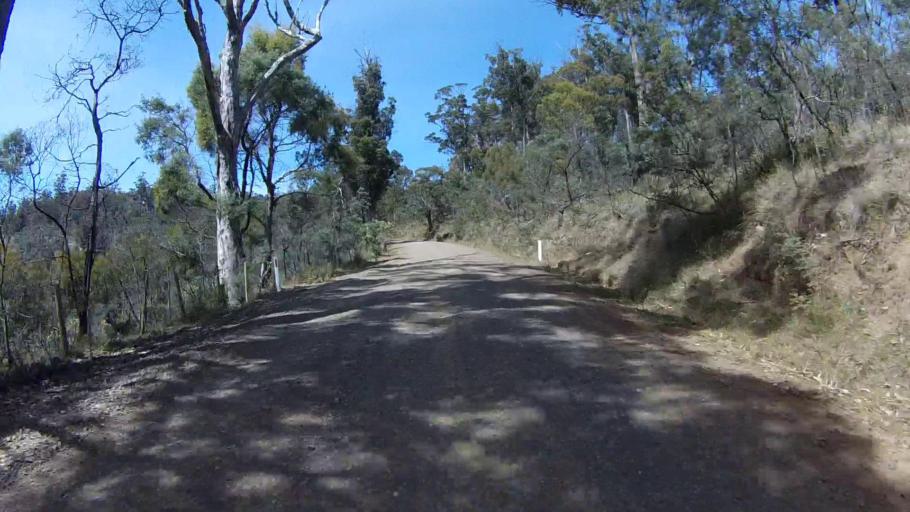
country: AU
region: Tasmania
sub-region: Sorell
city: Sorell
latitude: -42.6502
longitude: 147.7439
